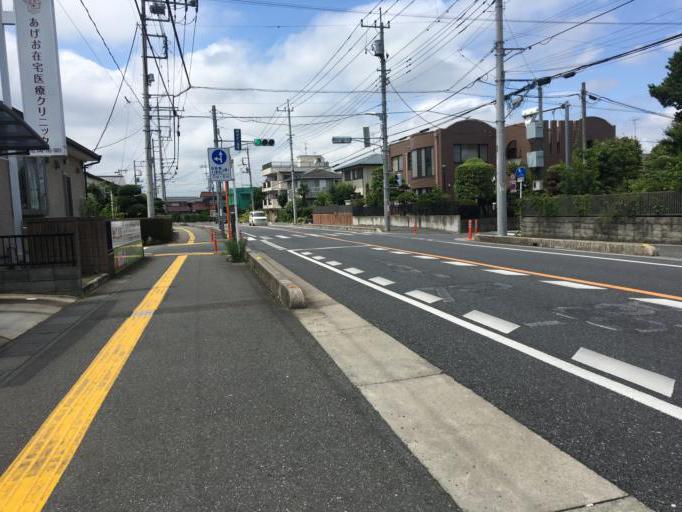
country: JP
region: Saitama
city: Okegawa
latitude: 35.9932
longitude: 139.5737
